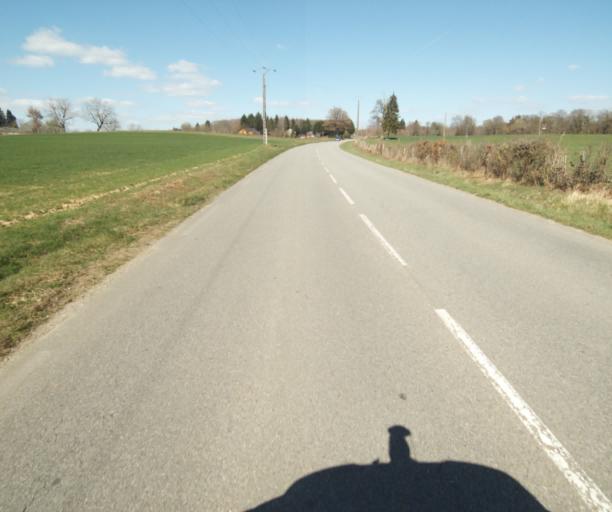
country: FR
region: Limousin
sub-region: Departement de la Correze
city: Saint-Mexant
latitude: 45.2939
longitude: 1.6695
